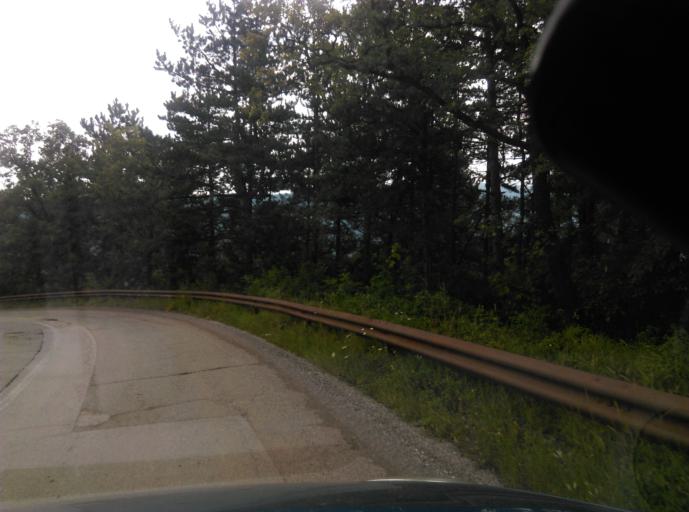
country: BG
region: Sofia-Capital
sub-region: Stolichna Obshtina
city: Sofia
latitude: 42.5897
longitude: 23.4057
